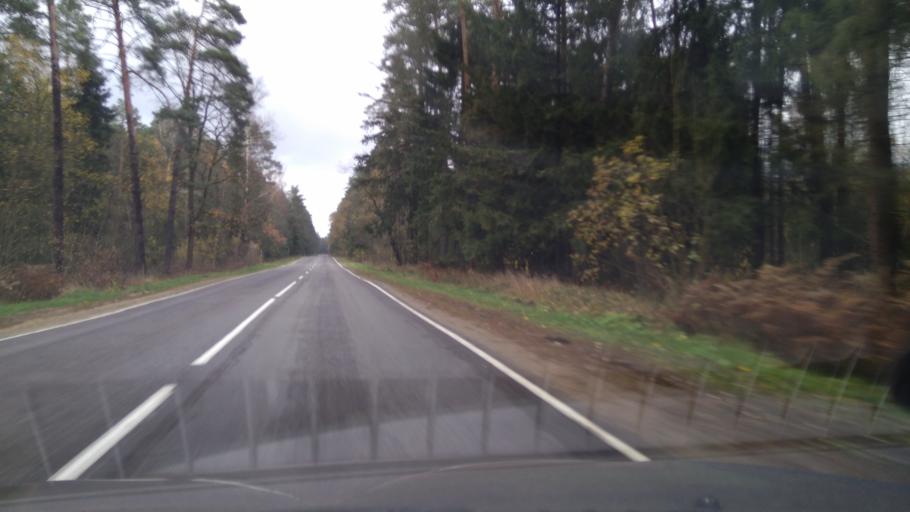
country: BY
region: Minsk
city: Slutsk
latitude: 53.2207
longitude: 27.5890
